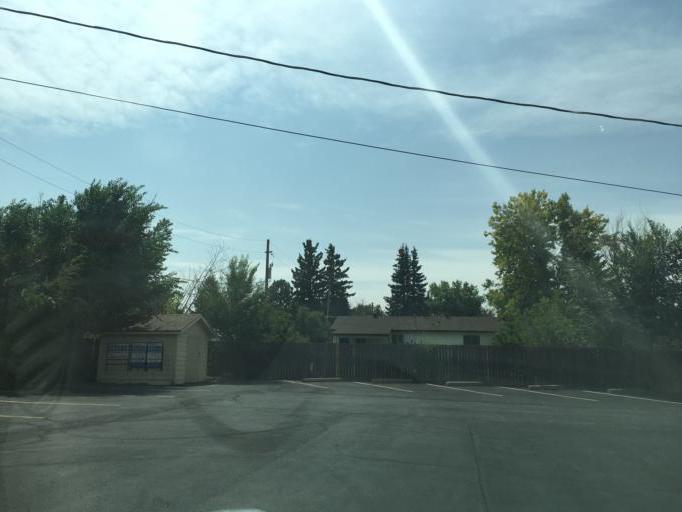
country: US
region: Colorado
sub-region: Adams County
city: Aurora
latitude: 39.7363
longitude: -104.7966
